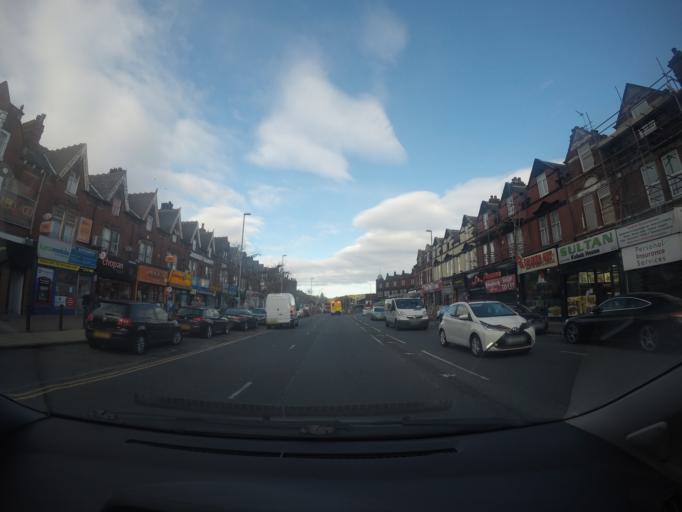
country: GB
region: England
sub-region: City and Borough of Leeds
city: Chapel Allerton
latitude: 53.8160
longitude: -1.5181
